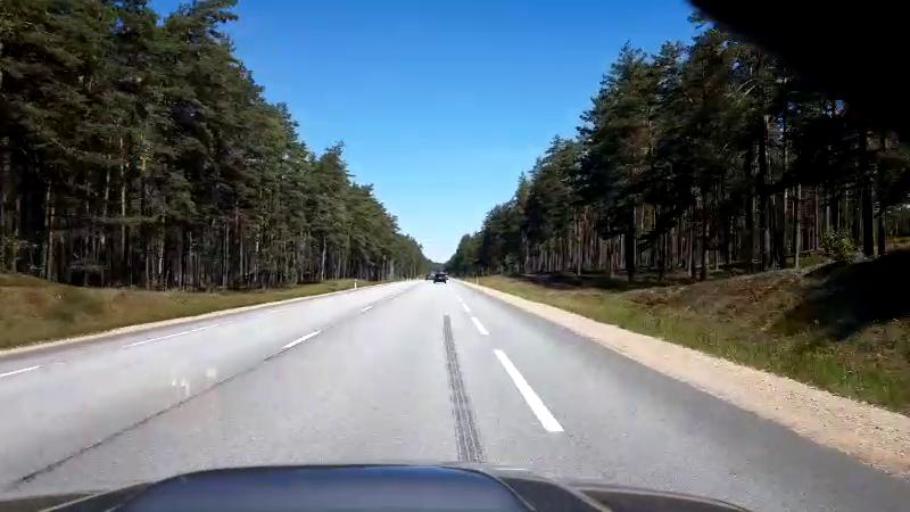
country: LV
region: Carnikava
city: Carnikava
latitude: 57.1662
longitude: 24.3447
